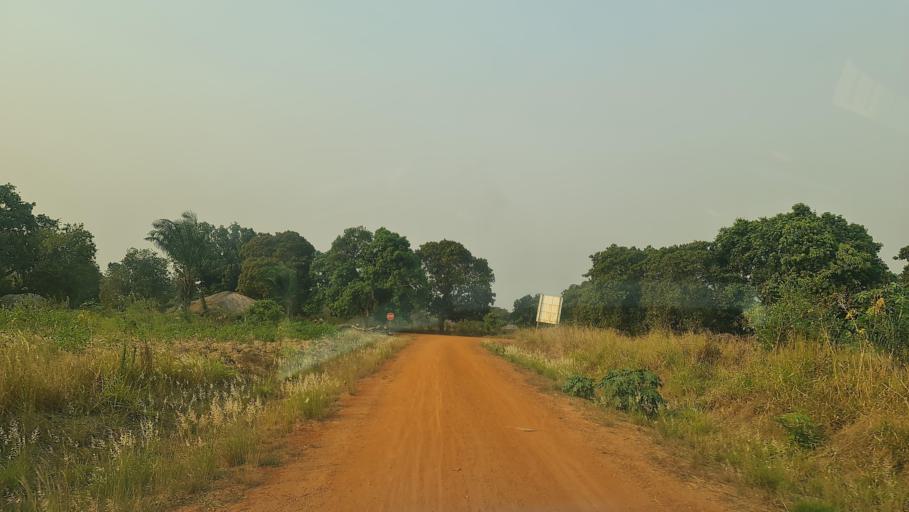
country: MZ
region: Zambezia
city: Quelimane
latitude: -17.0965
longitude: 37.1888
